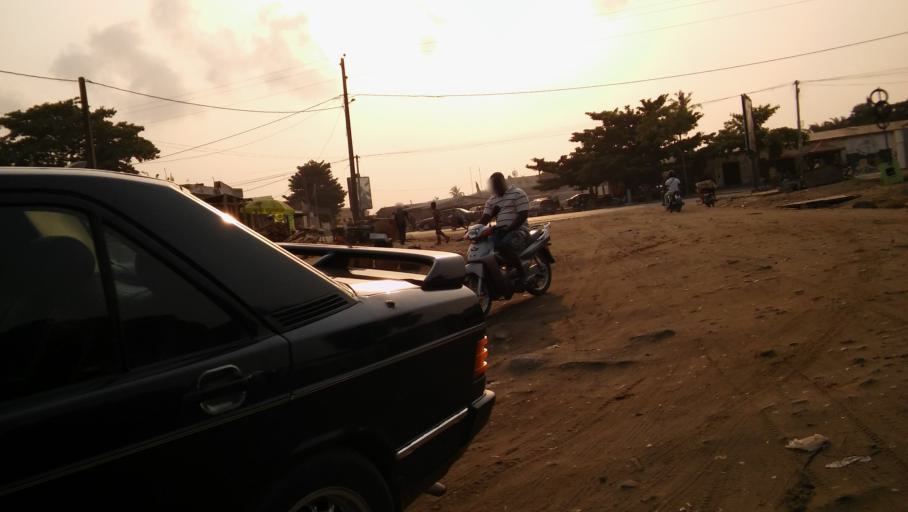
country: BJ
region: Littoral
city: Cotonou
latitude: 6.3881
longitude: 2.3851
